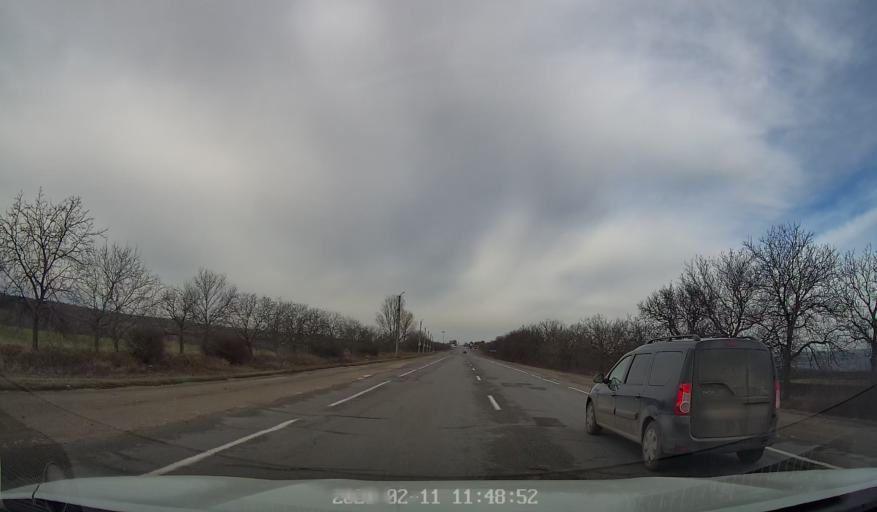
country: MD
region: Balti
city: Balti
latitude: 47.8430
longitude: 27.7980
